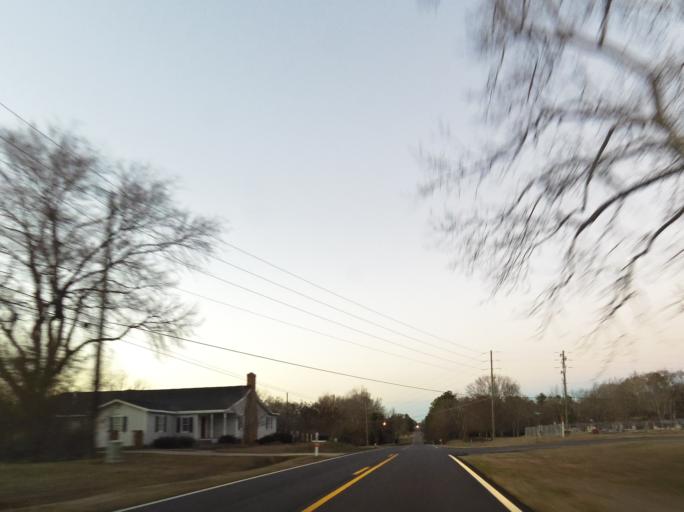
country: US
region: Georgia
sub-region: Peach County
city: Byron
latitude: 32.6231
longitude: -83.7574
